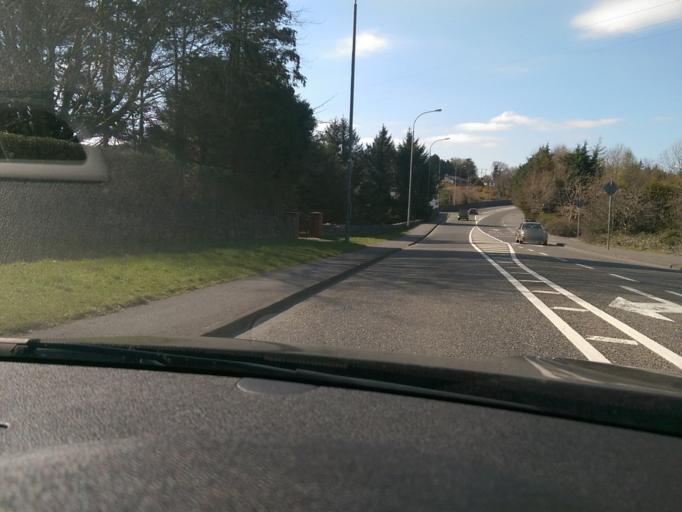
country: IE
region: Connaught
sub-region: County Galway
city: Gaillimh
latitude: 53.2913
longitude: -9.0816
